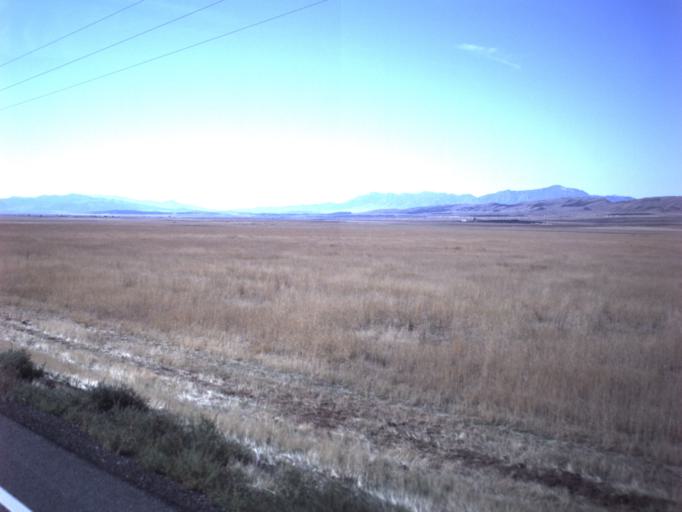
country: US
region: Utah
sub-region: Juab County
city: Nephi
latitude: 39.6142
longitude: -111.8619
